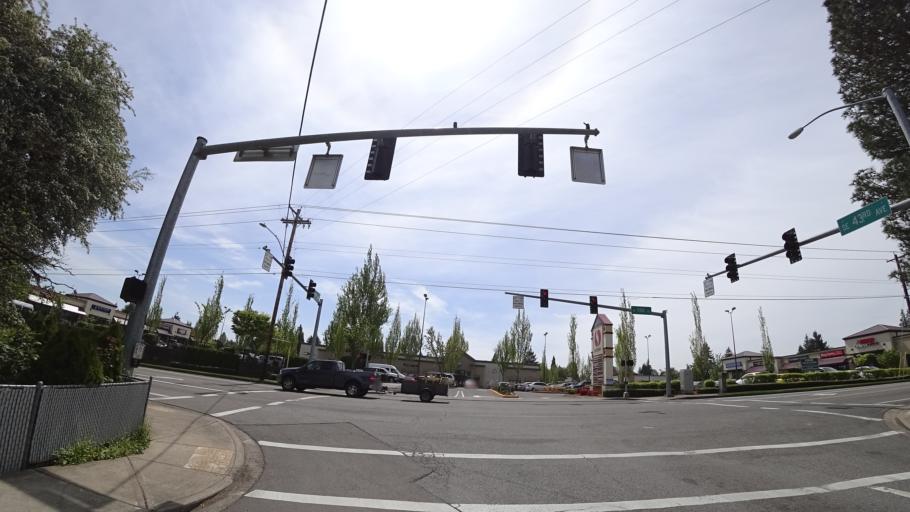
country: US
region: Oregon
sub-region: Clackamas County
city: Milwaukie
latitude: 45.4482
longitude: -122.6185
